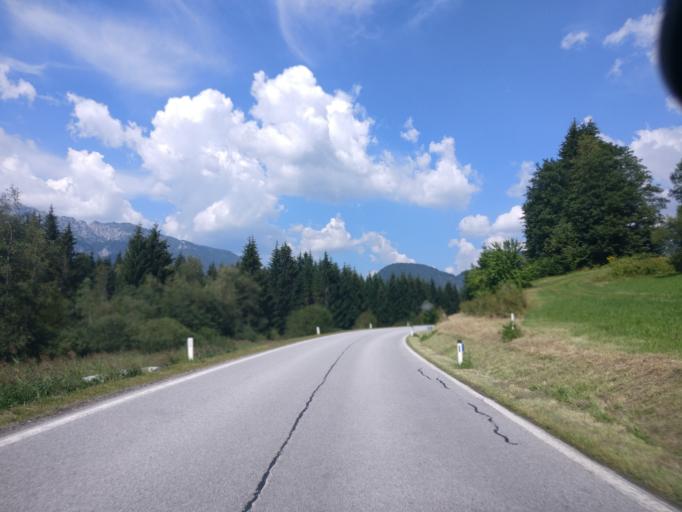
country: AT
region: Styria
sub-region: Politischer Bezirk Liezen
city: Hall bei Admont
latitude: 47.5780
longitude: 14.4864
